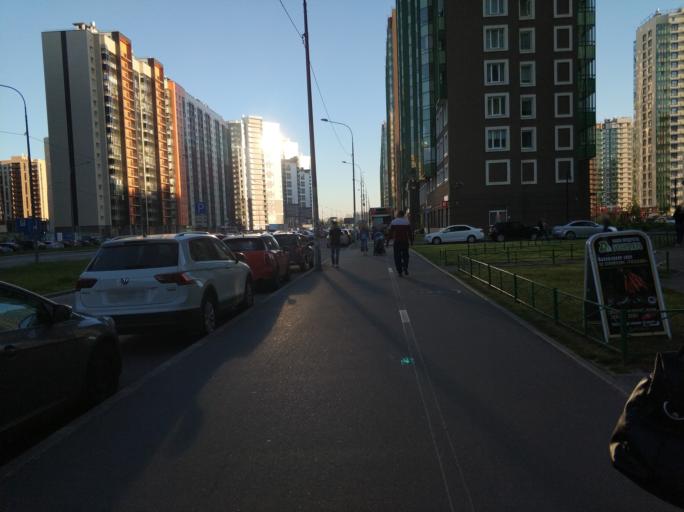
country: RU
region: Leningrad
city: Murino
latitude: 60.0564
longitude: 30.4276
